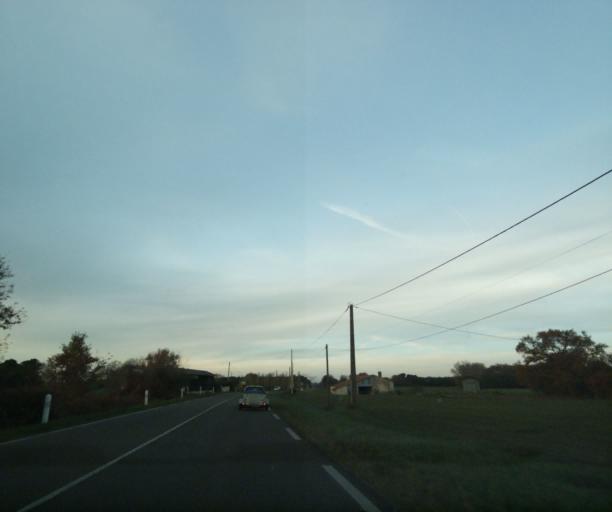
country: FR
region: Aquitaine
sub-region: Departement de la Gironde
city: Langon
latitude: 44.4979
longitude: -0.2373
